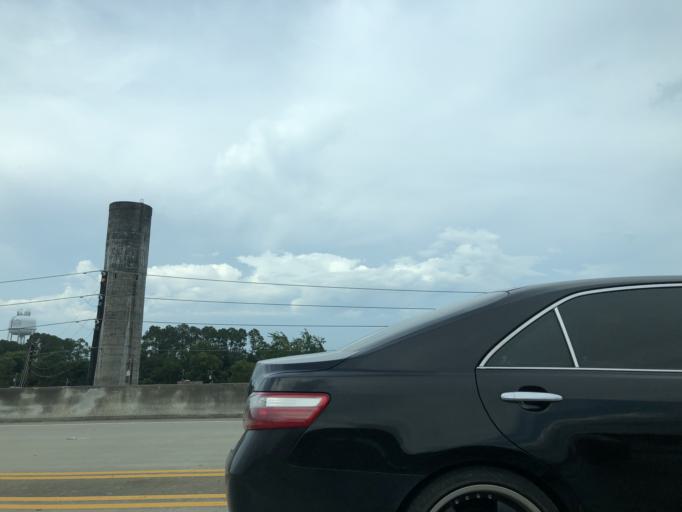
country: US
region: Georgia
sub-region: Wayne County
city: Jesup
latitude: 31.6070
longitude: -81.8804
